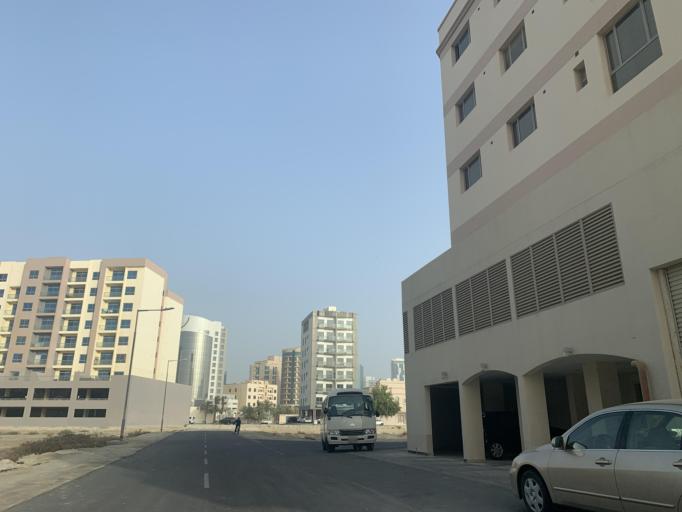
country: BH
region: Manama
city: Jidd Hafs
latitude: 26.2423
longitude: 50.5313
